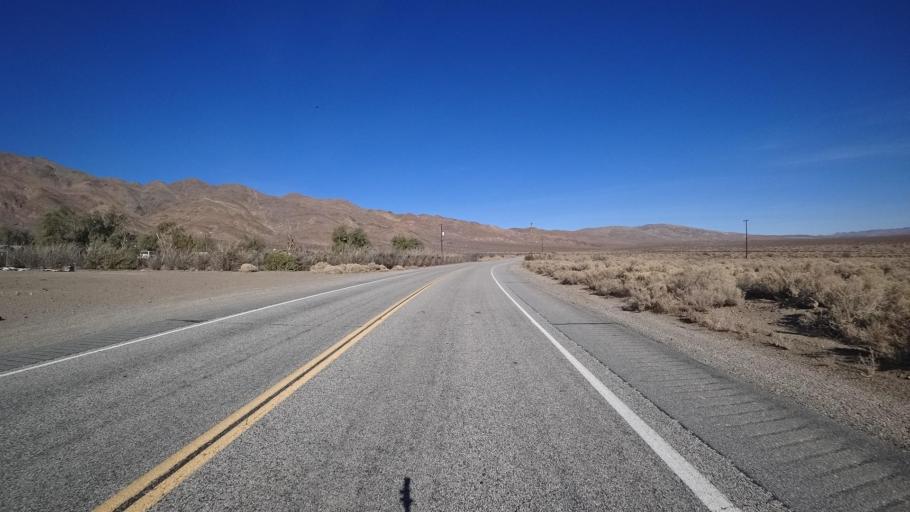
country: US
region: California
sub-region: Kern County
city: China Lake Acres
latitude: 35.4033
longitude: -117.7900
